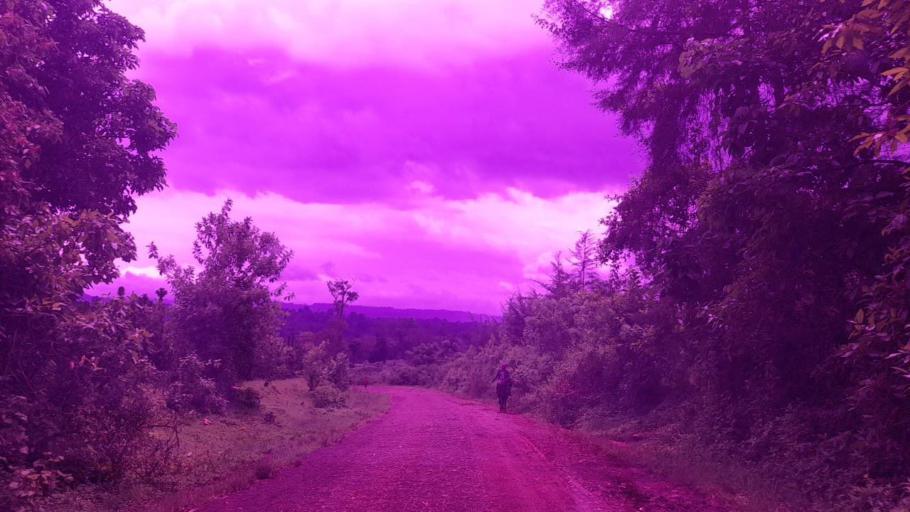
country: ET
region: Southern Nations, Nationalities, and People's Region
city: Tippi
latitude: 7.6328
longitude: 35.5723
